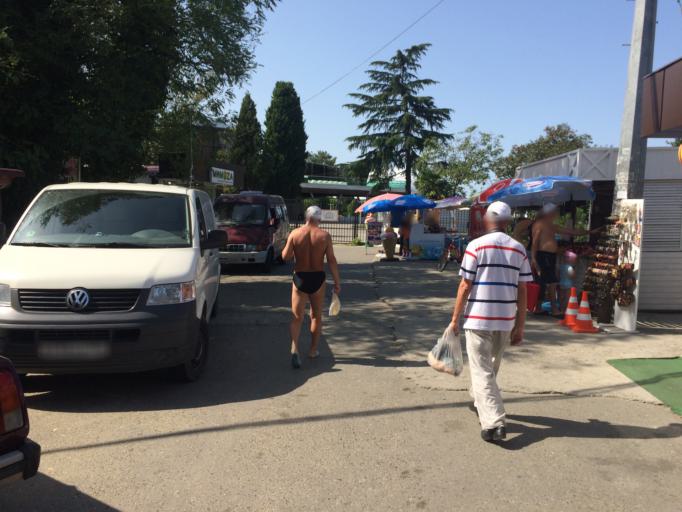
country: RU
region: Krasnodarskiy
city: Adler
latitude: 43.3985
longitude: 39.9656
